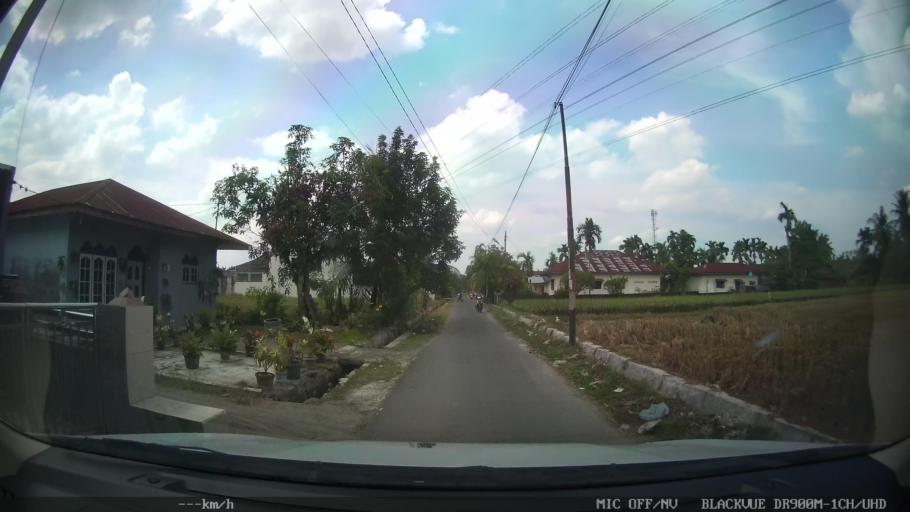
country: ID
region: North Sumatra
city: Binjai
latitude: 3.6240
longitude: 98.5165
